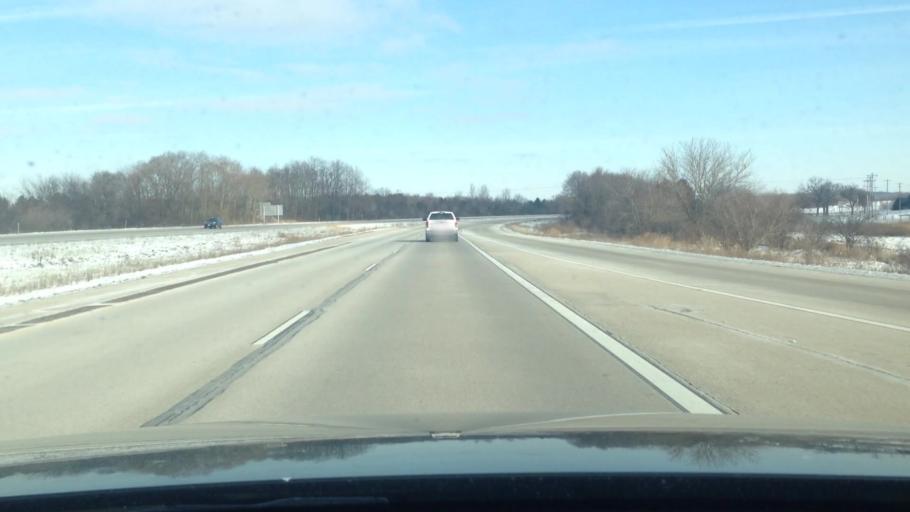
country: US
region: Wisconsin
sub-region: Walworth County
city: East Troy
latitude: 42.7959
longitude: -88.3832
